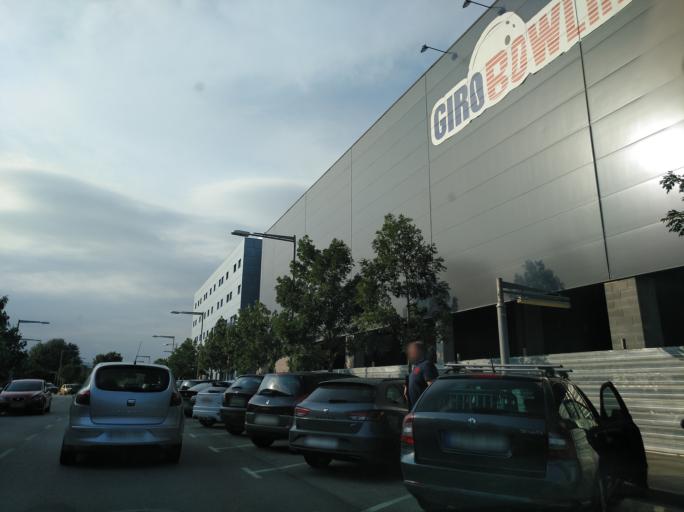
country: ES
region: Catalonia
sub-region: Provincia de Girona
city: Salt
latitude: 41.9669
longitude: 2.7837
